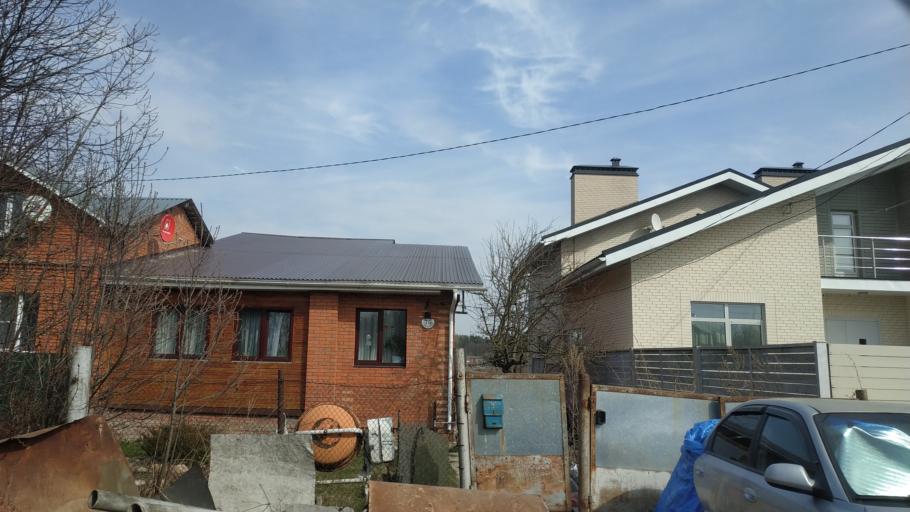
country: RU
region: Moskovskaya
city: Voskresensk
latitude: 55.3415
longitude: 38.6187
